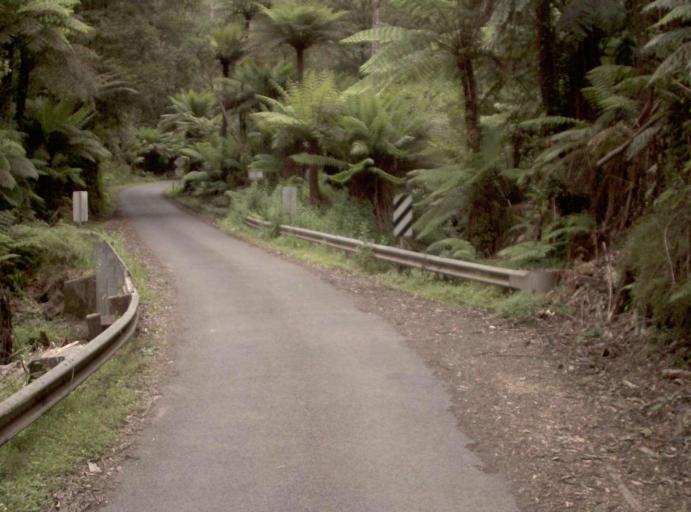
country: AU
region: Victoria
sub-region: Latrobe
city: Traralgon
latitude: -38.4506
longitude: 146.5394
